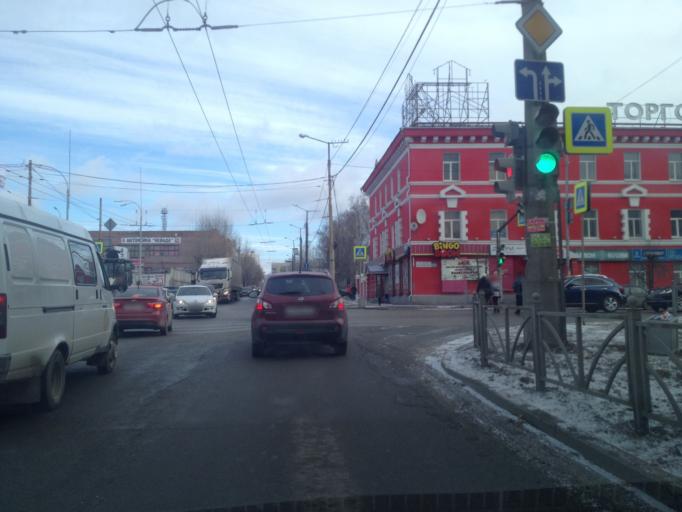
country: RU
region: Sverdlovsk
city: Yekaterinburg
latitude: 56.8249
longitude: 60.5671
